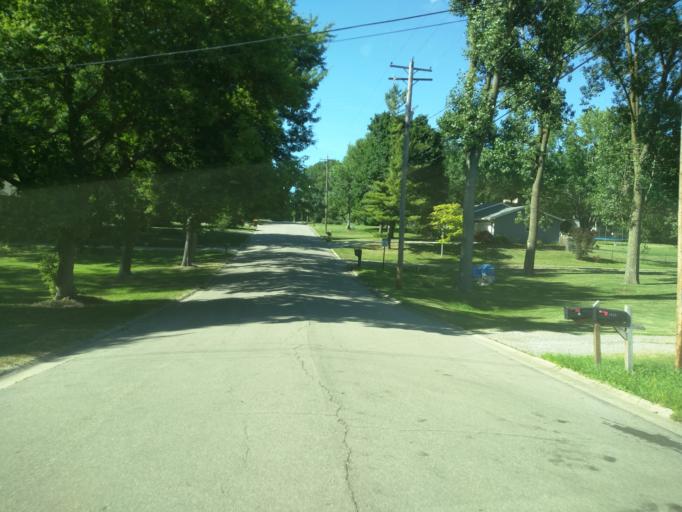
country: US
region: Michigan
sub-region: Eaton County
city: Waverly
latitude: 42.7458
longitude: -84.6361
